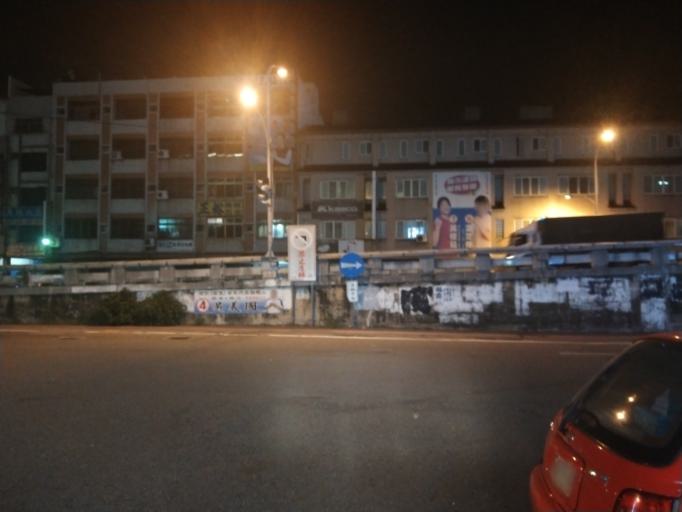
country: TW
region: Taiwan
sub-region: Changhua
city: Chang-hua
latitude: 24.0645
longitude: 120.5345
